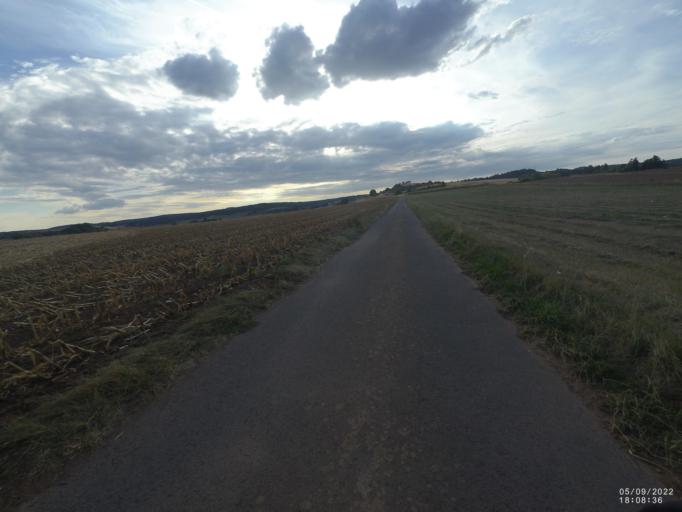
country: DE
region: Rheinland-Pfalz
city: Basberg
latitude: 50.2927
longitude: 6.5878
